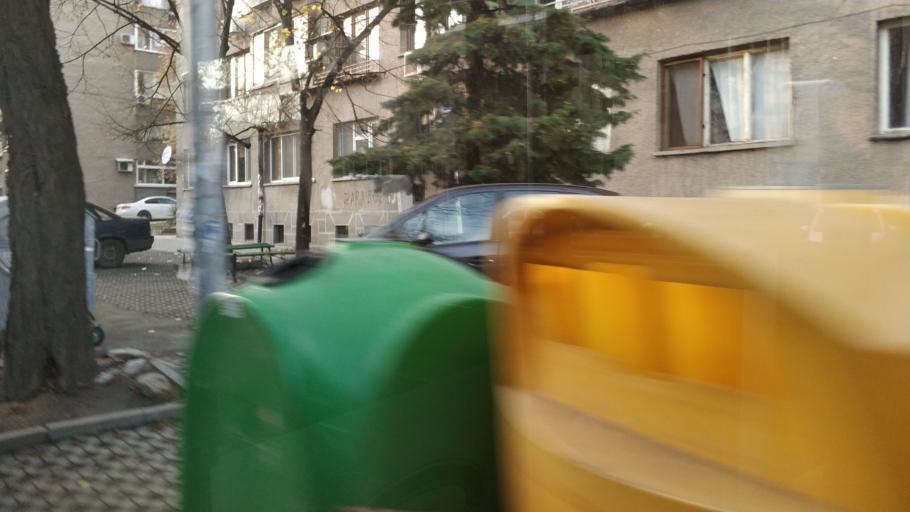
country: BG
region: Stara Zagora
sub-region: Obshtina Stara Zagora
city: Stara Zagora
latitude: 42.4188
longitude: 25.6256
